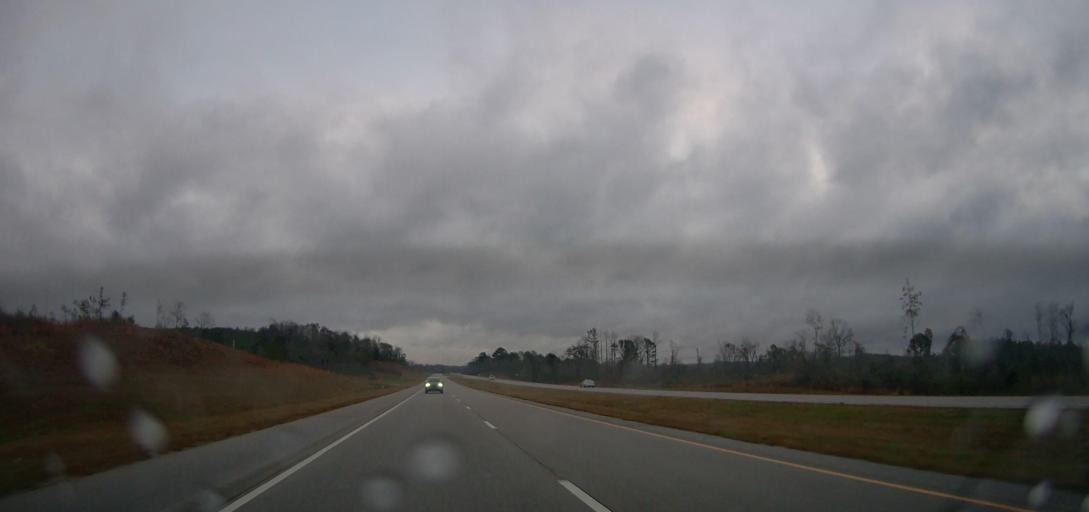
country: US
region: Alabama
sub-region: Bibb County
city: Centreville
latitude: 32.9459
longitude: -87.0915
